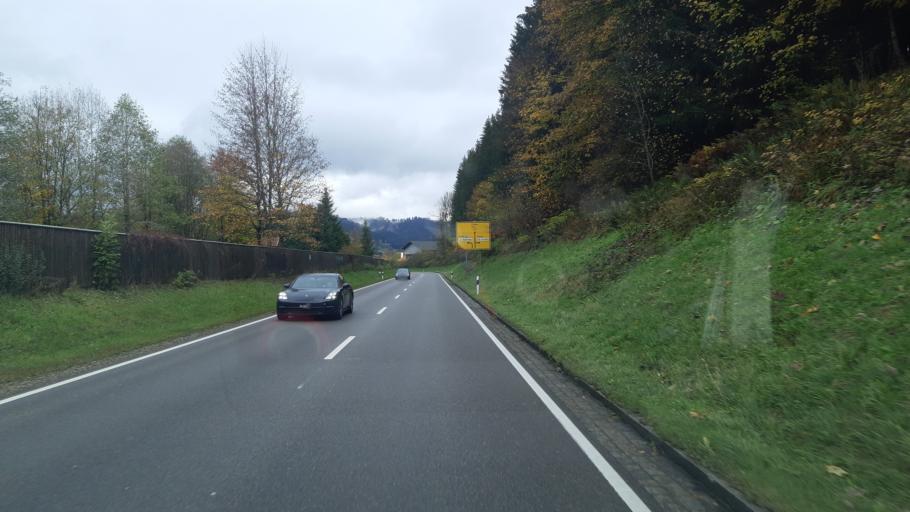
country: DE
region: Bavaria
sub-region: Swabia
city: Maierhofen
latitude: 47.6534
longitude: 10.0862
